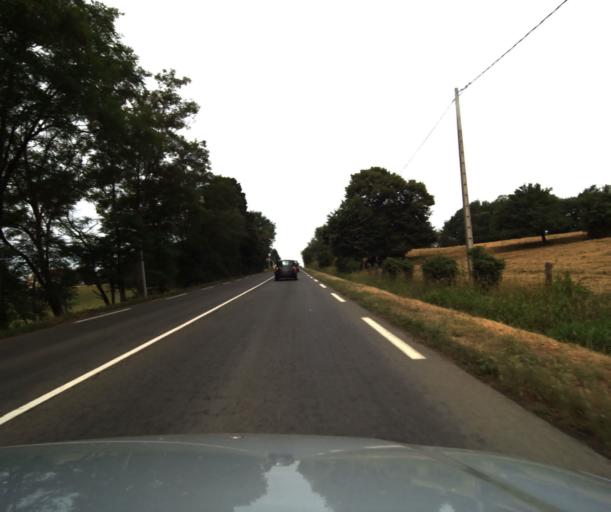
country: FR
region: Midi-Pyrenees
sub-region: Departement du Gers
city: Mielan
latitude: 43.4197
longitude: 0.2548
